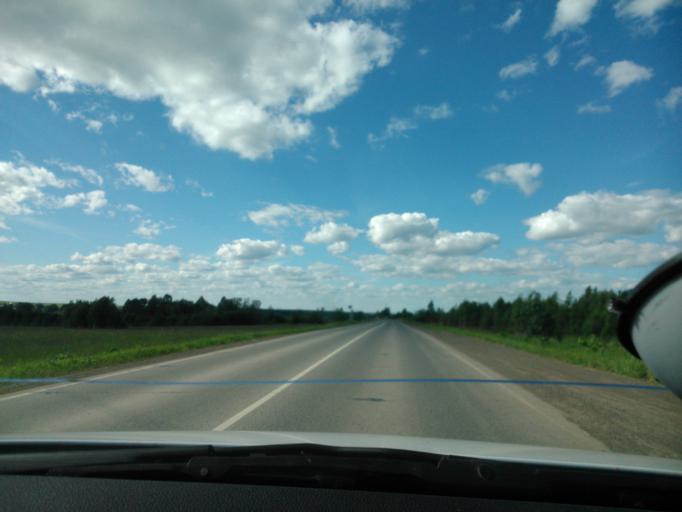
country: RU
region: Perm
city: Ust'-Kachka
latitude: 57.9267
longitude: 55.7621
